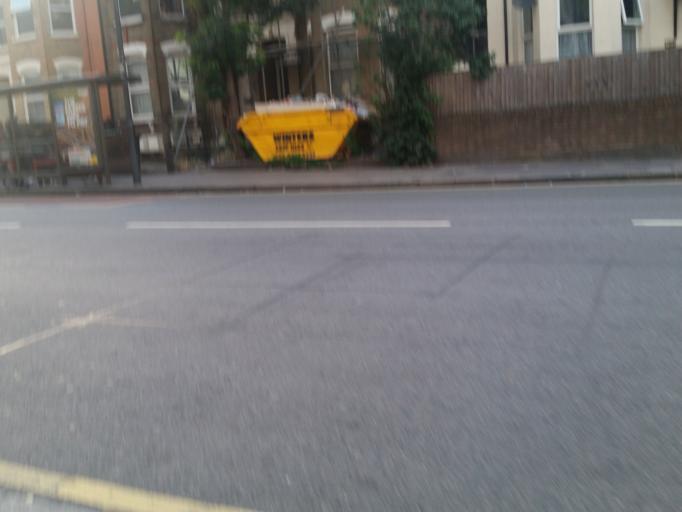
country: GB
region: England
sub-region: Greater London
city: Wood Green
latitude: 51.5974
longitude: -0.1076
